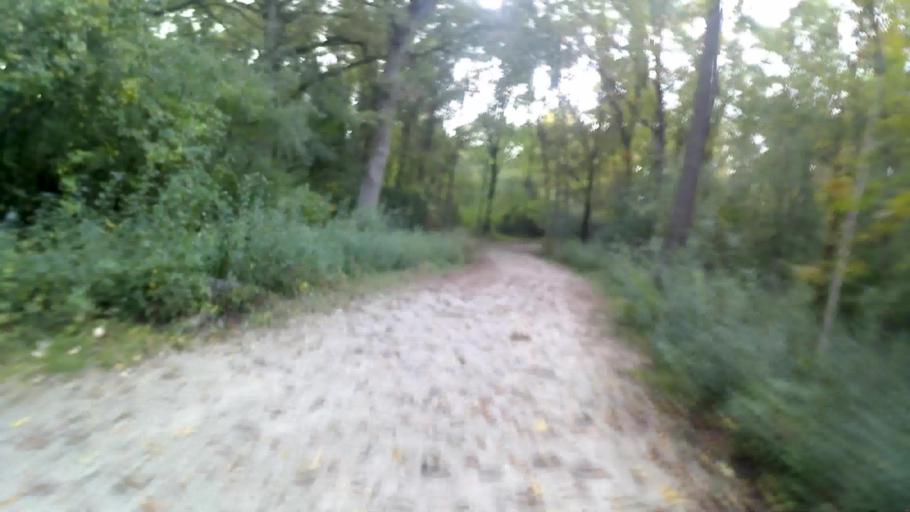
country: US
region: Illinois
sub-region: DuPage County
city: Naperville
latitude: 41.8167
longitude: -88.1260
